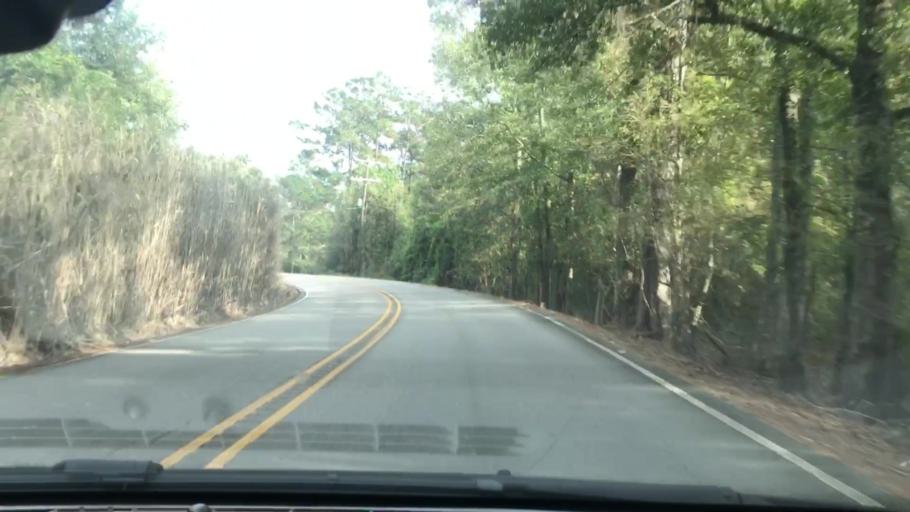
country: US
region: Louisiana
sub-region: Saint Tammany Parish
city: Abita Springs
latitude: 30.5327
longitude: -89.8818
